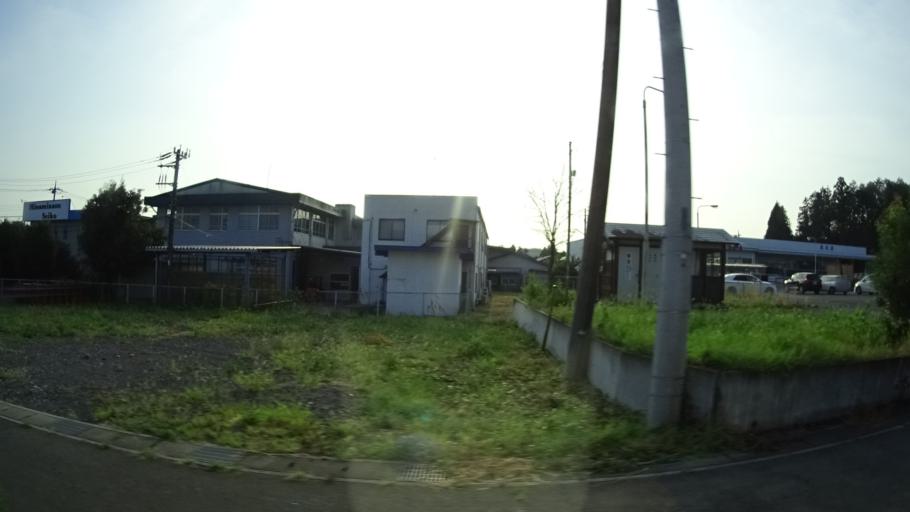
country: JP
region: Tochigi
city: Karasuyama
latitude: 36.6372
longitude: 140.1527
